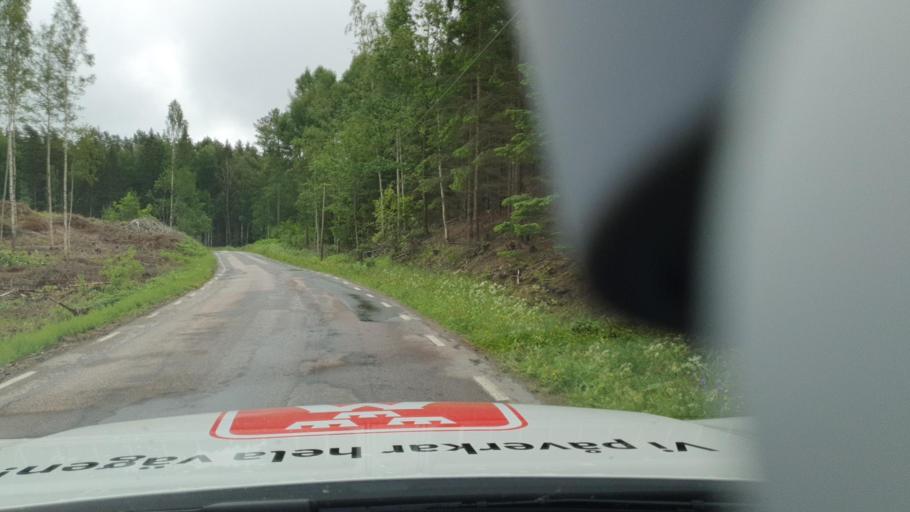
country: SE
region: Vaestra Goetaland
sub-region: Gullspangs Kommun
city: Gullspang
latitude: 59.0349
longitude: 14.1589
